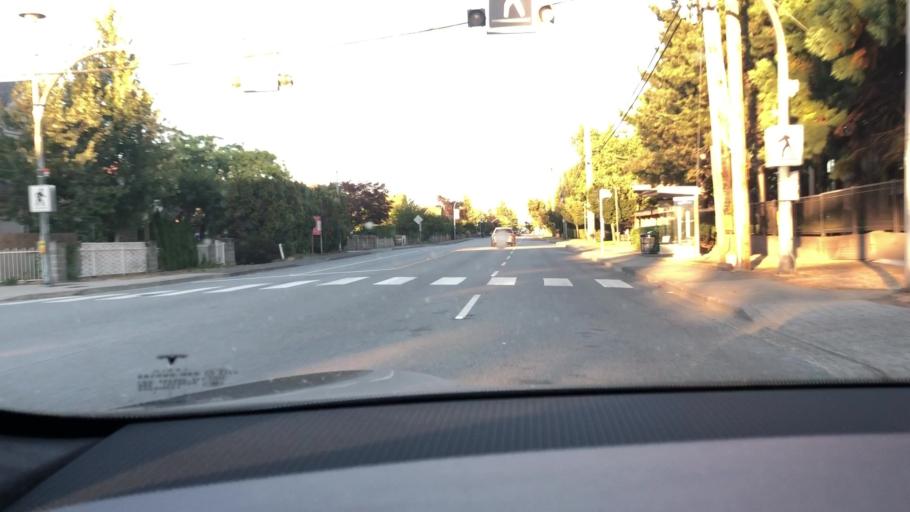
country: CA
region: British Columbia
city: Richmond
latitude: 49.1555
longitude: -123.1563
